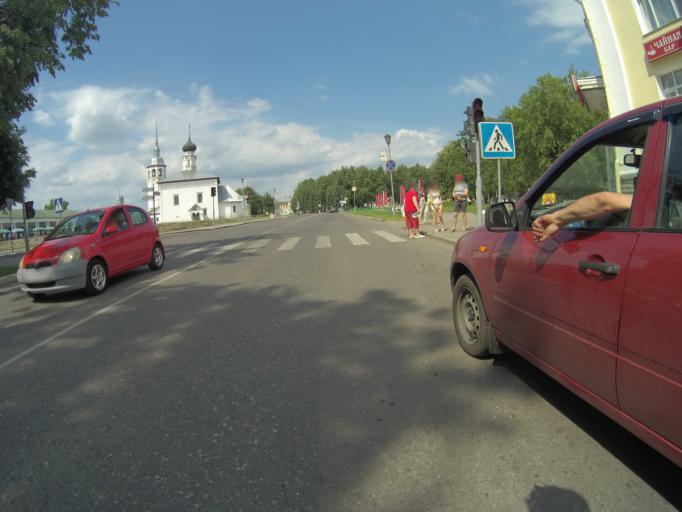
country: RU
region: Vladimir
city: Suzdal'
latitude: 56.4187
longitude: 40.4492
